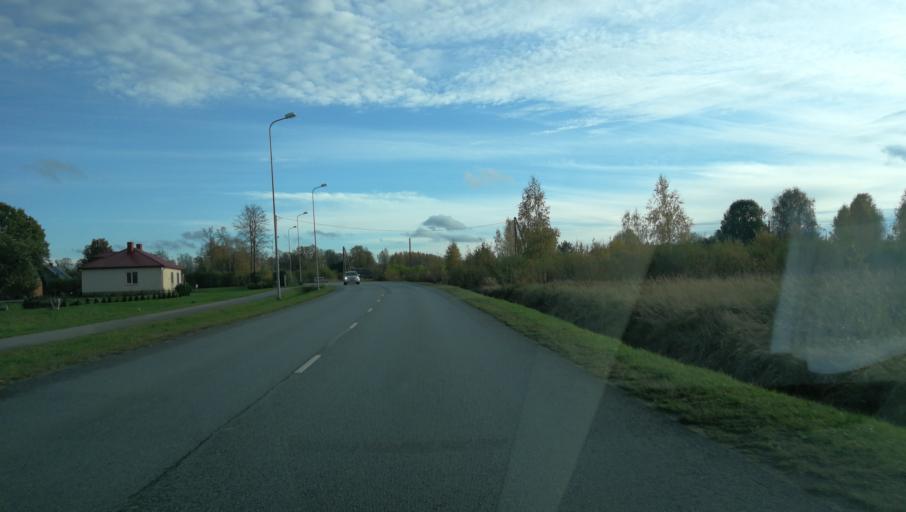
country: LV
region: Cesu Rajons
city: Cesis
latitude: 57.2996
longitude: 25.2457
